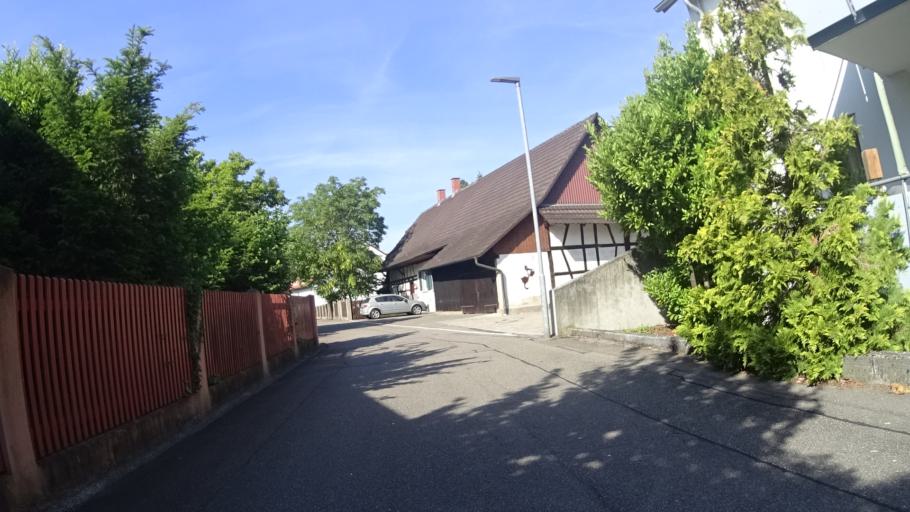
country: DE
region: Baden-Wuerttemberg
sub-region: Freiburg Region
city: Kehl
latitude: 48.5570
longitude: 7.8362
